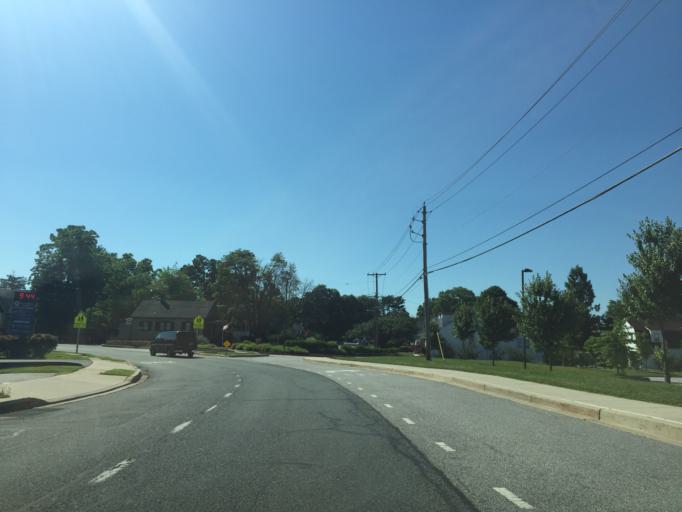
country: US
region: Maryland
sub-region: Harford County
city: Bel Air
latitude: 39.5314
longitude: -76.3458
